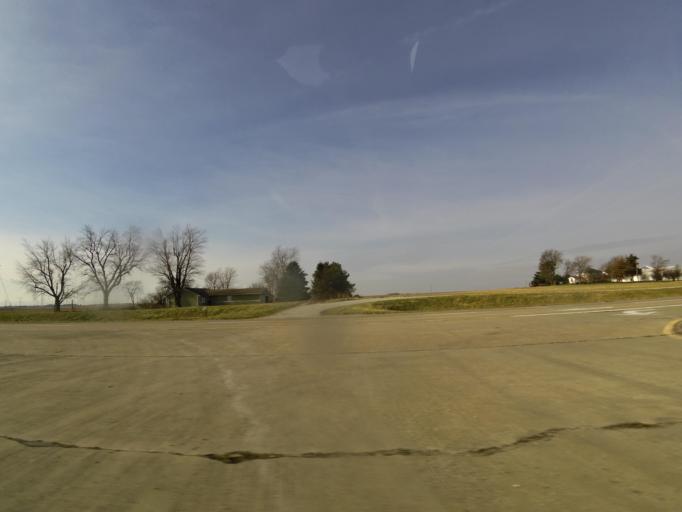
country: US
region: Illinois
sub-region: Macon County
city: Maroa
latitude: 40.0663
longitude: -88.9657
